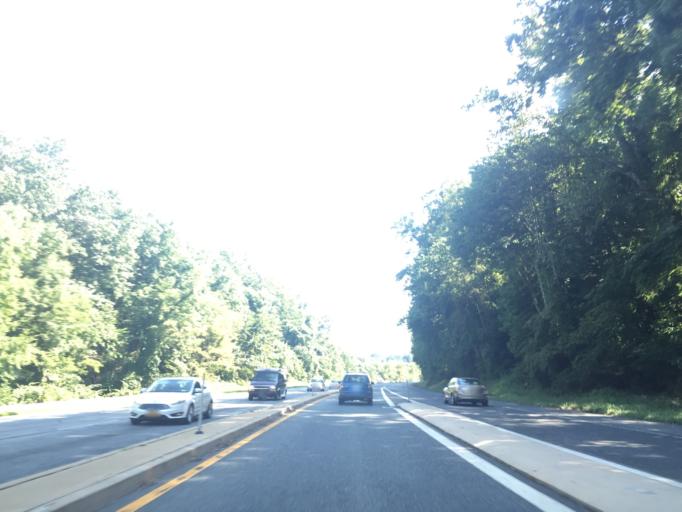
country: US
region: Maryland
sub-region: Harford County
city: North Bel Air
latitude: 39.5324
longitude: -76.3677
